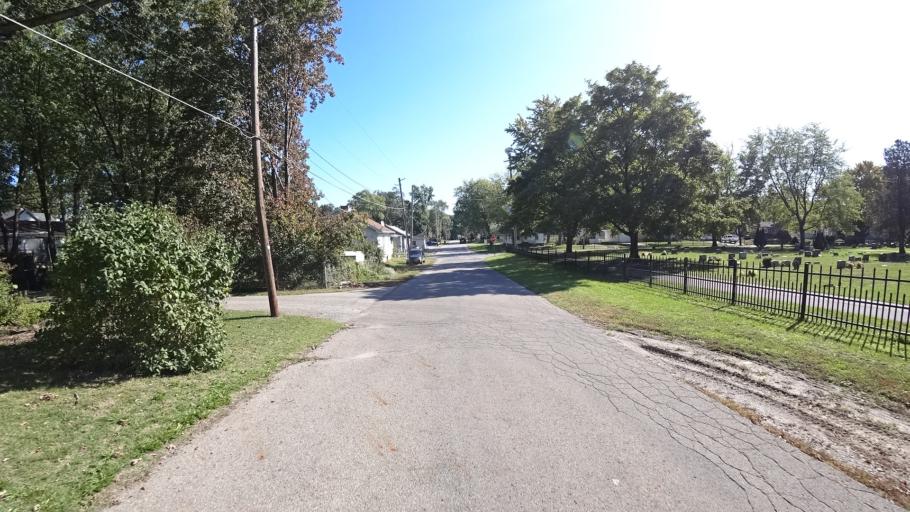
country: US
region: Indiana
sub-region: LaPorte County
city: Michigan City
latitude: 41.7048
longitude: -86.8812
